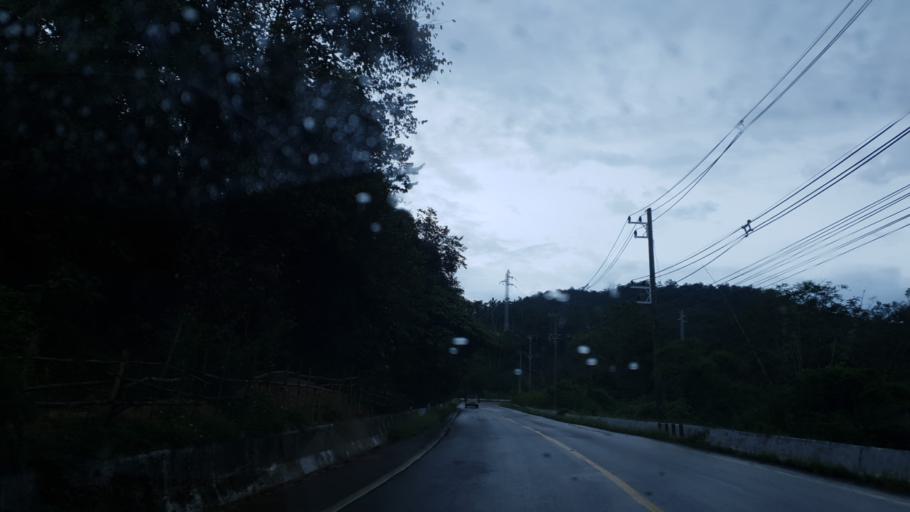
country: TH
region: Mae Hong Son
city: Ban Huai I Huak
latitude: 18.1449
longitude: 98.2036
